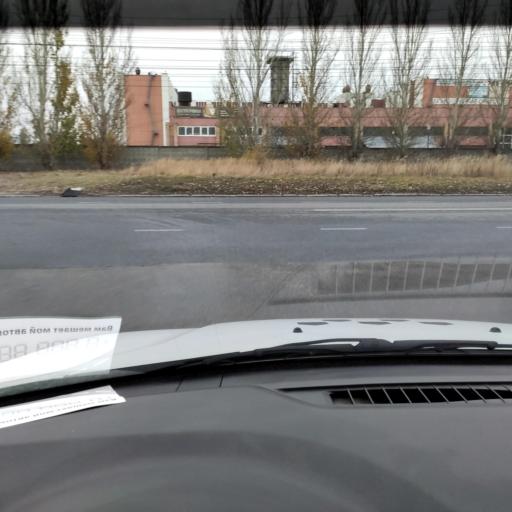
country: RU
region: Samara
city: Tol'yatti
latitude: 53.5589
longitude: 49.2949
